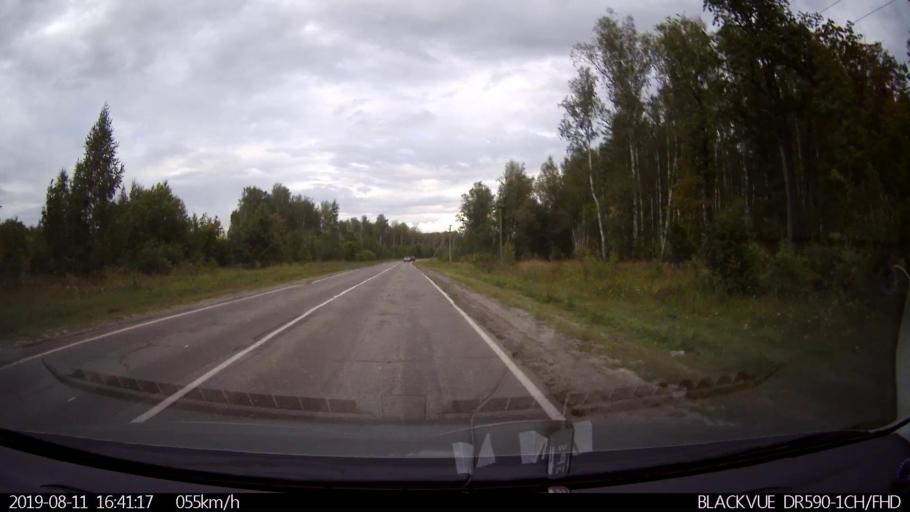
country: RU
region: Ulyanovsk
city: Mayna
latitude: 54.1521
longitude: 47.6517
